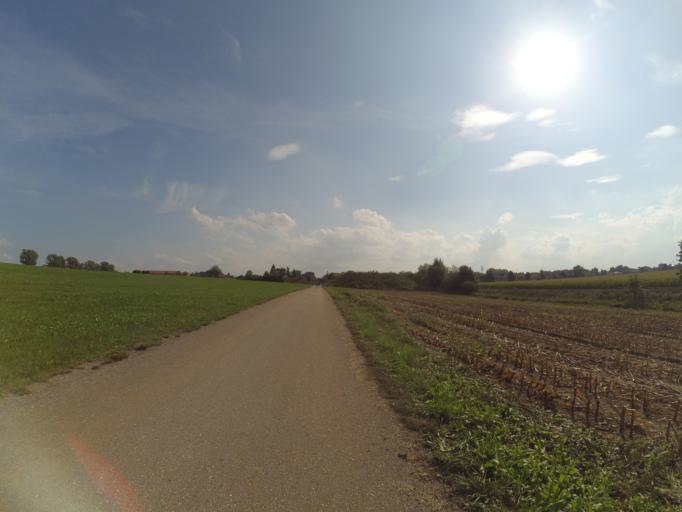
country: DE
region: Bavaria
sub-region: Swabia
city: Buchloe
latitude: 48.0506
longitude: 10.7272
